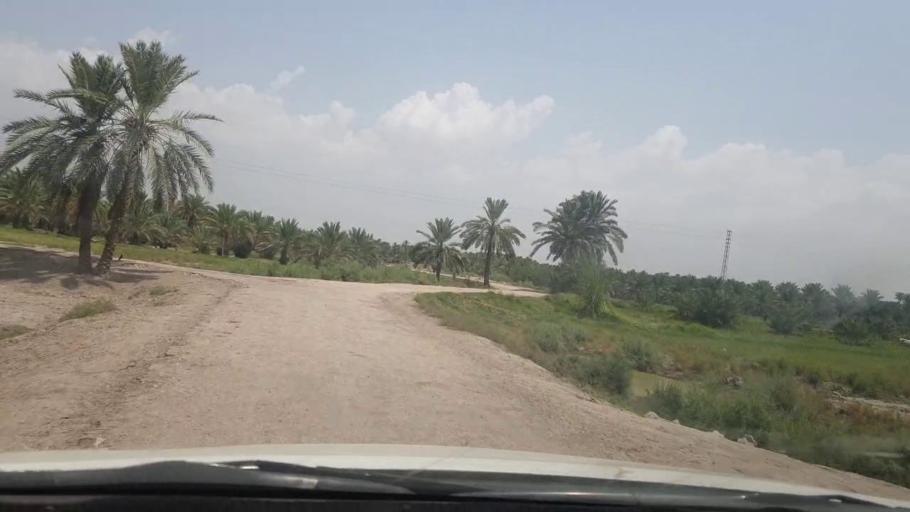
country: PK
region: Sindh
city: Khairpur
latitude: 27.5480
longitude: 68.8231
